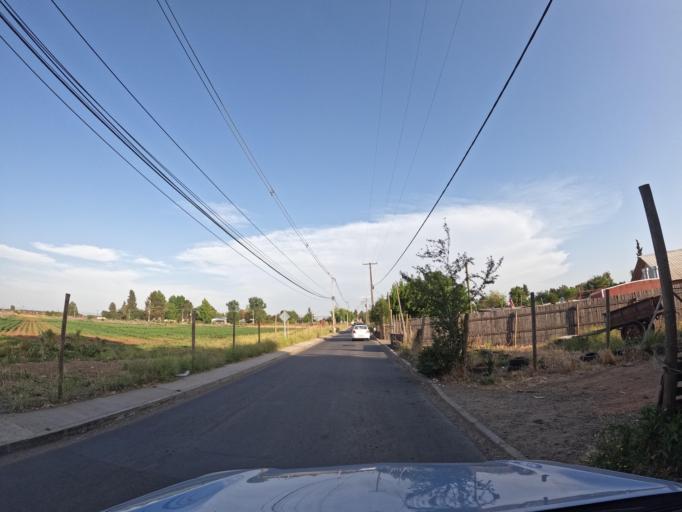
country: CL
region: Maule
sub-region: Provincia de Talca
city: Talca
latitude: -35.4475
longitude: -71.6198
